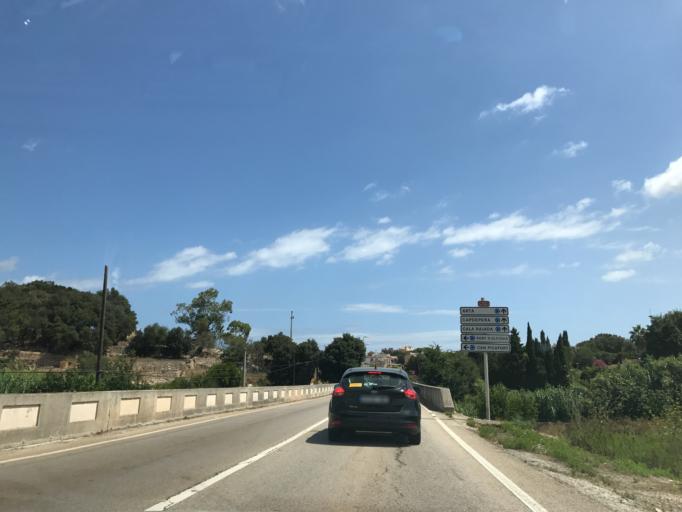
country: ES
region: Balearic Islands
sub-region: Illes Balears
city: Arta
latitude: 39.6878
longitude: 3.3447
